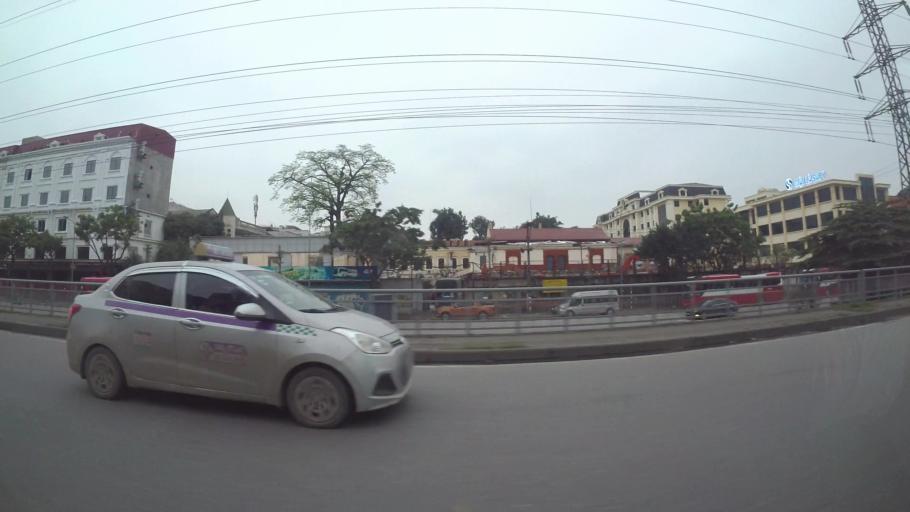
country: VN
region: Ha Noi
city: Hoan Kiem
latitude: 21.0233
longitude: 105.8610
